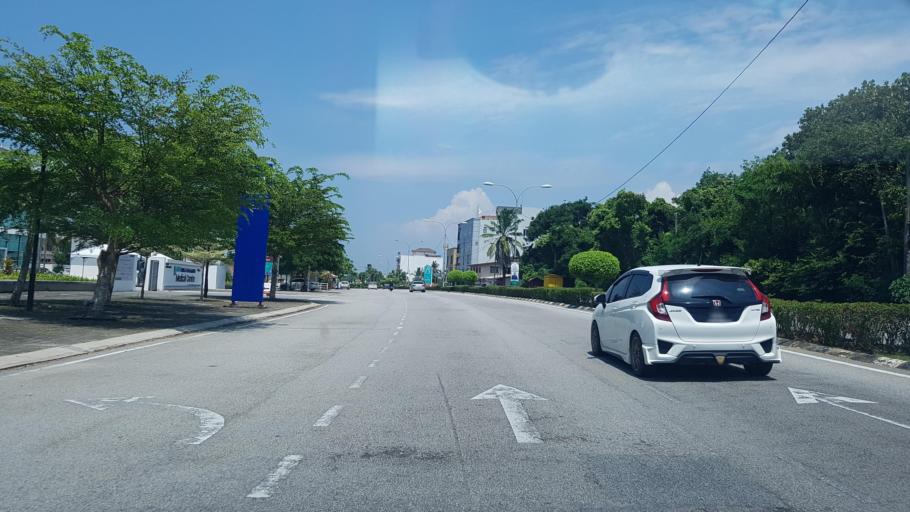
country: MY
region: Terengganu
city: Kuala Terengganu
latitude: 5.3140
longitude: 103.1551
